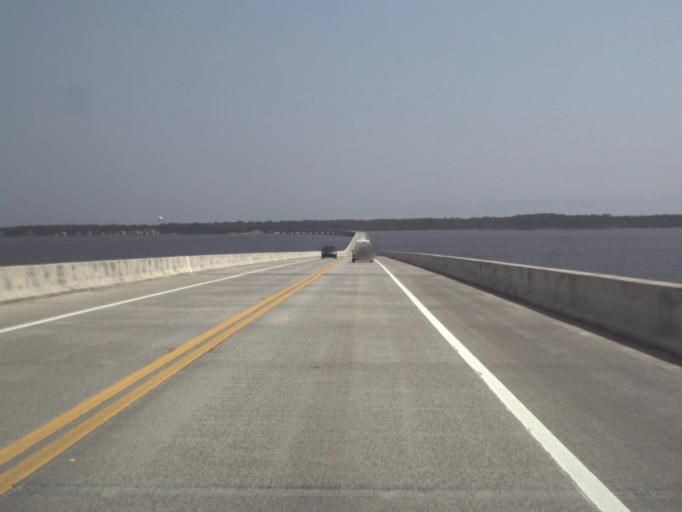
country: US
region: Florida
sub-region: Santa Rosa County
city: Oriole Beach
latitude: 30.4148
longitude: -87.0873
